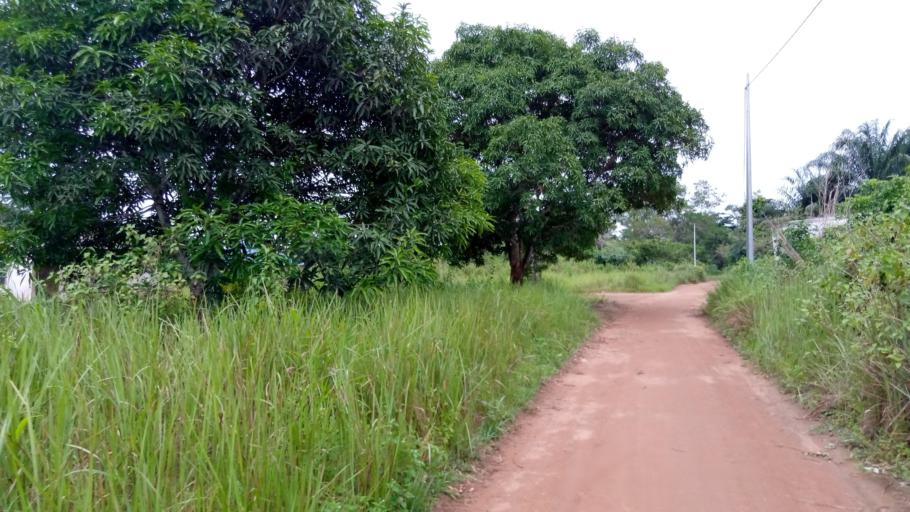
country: SL
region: Southern Province
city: Rotifunk
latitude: 8.1890
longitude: -12.5709
